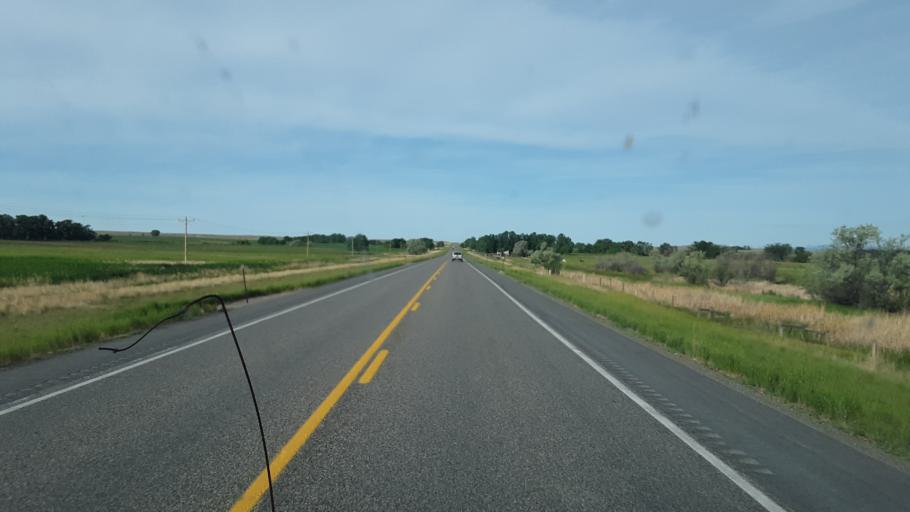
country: US
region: Wyoming
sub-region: Fremont County
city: Riverton
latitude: 43.1826
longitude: -108.2486
